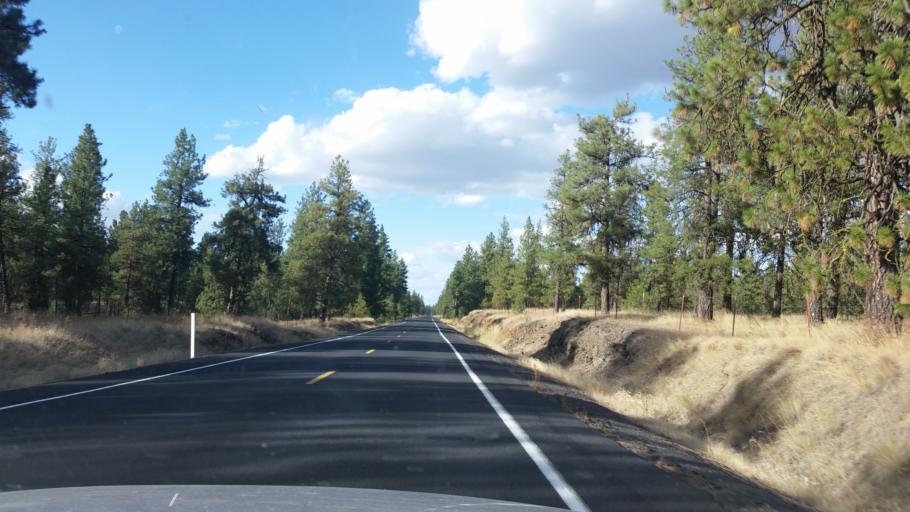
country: US
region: Washington
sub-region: Spokane County
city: Cheney
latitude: 47.4105
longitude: -117.5689
